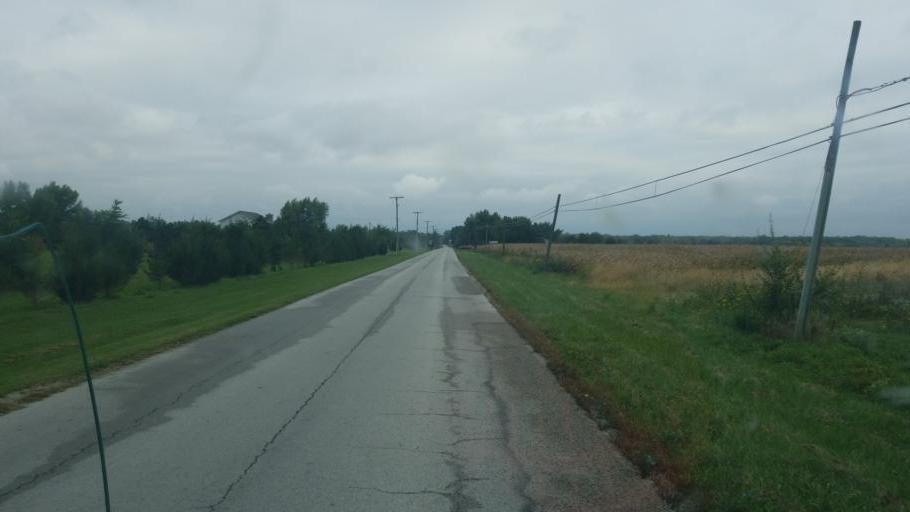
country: US
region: Ohio
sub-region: Wood County
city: Bowling Green
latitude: 41.2873
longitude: -83.6695
